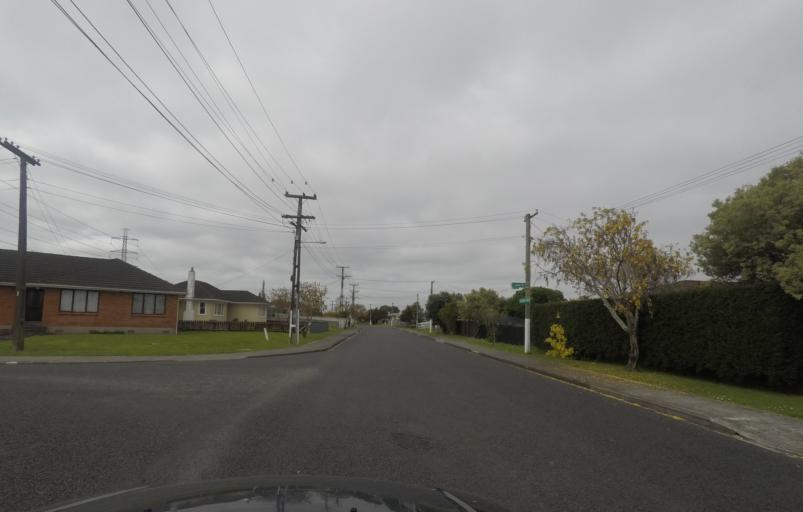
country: NZ
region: Auckland
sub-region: Auckland
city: Manukau City
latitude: -36.9585
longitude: 174.8644
